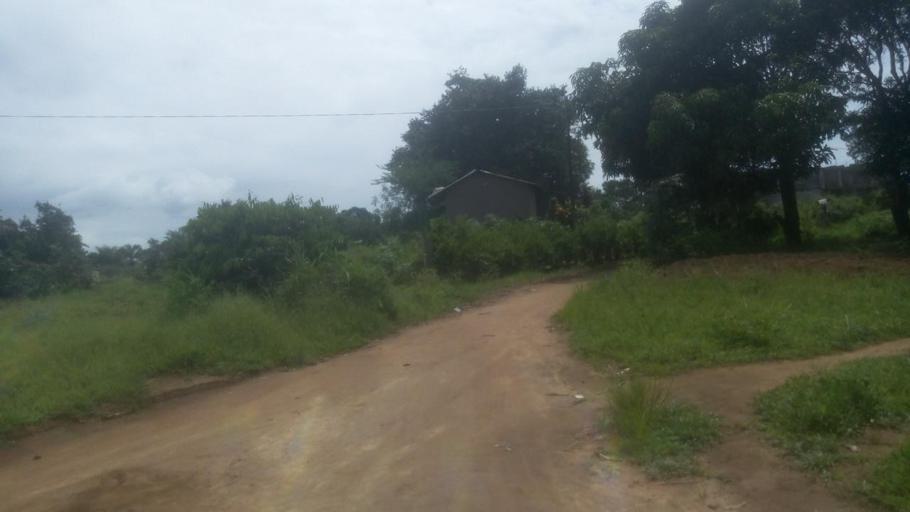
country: SL
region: Northern Province
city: Masoyila
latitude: 8.5310
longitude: -13.1498
